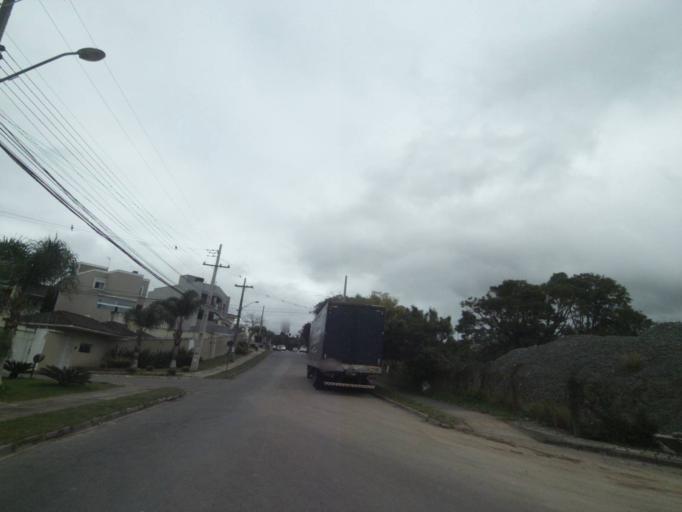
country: BR
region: Parana
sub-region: Curitiba
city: Curitiba
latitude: -25.5060
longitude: -49.2907
